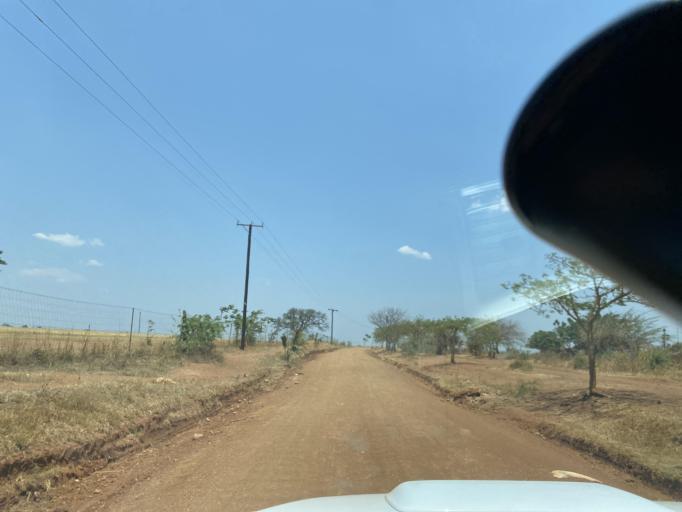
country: ZM
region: Lusaka
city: Lusaka
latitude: -15.4553
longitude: 28.0514
